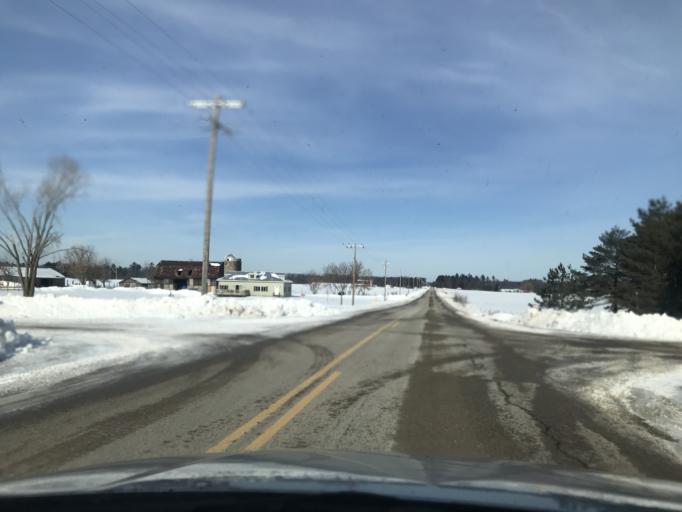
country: US
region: Wisconsin
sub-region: Oconto County
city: Oconto Falls
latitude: 45.1254
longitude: -88.1779
